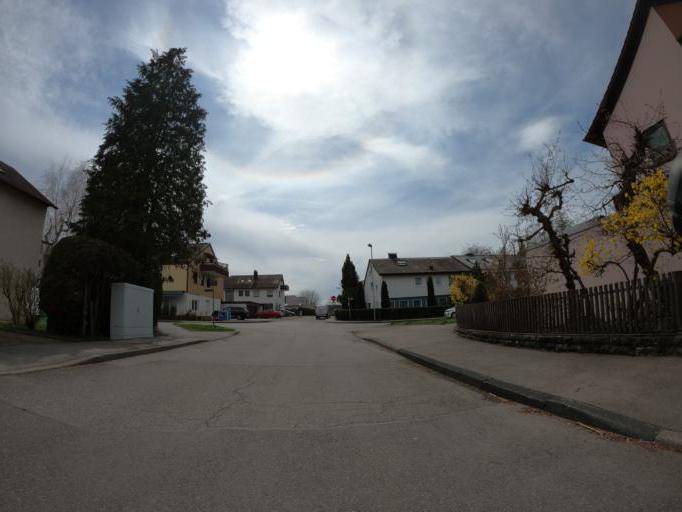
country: DE
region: Baden-Wuerttemberg
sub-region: Regierungsbezirk Stuttgart
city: Waldenbuch
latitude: 48.6411
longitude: 9.1381
